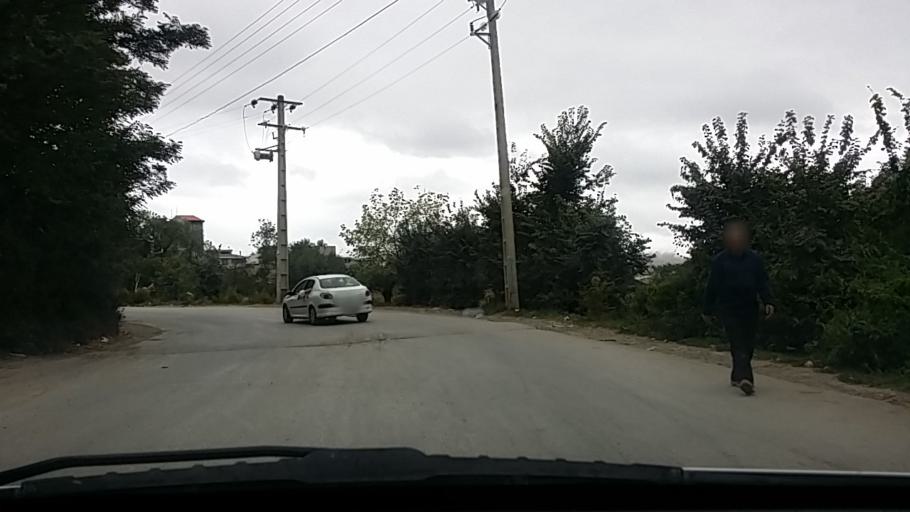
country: IR
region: Mazandaran
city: `Abbasabad
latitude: 36.5039
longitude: 51.1612
